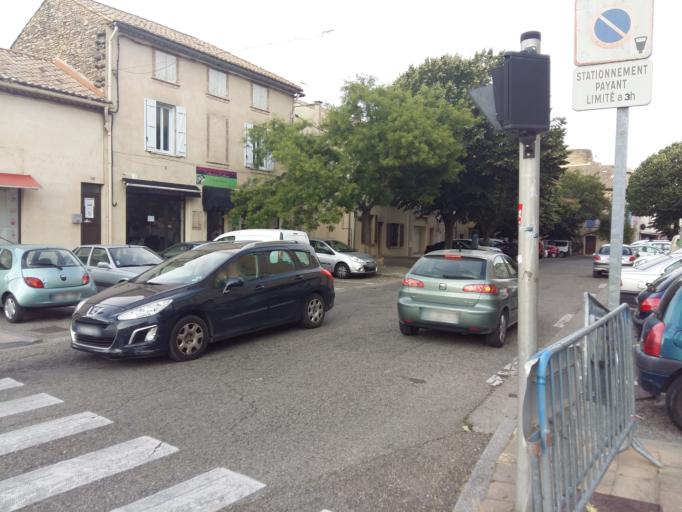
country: FR
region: Languedoc-Roussillon
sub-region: Departement du Gard
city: Bagnols-sur-Ceze
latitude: 44.1625
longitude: 4.6173
